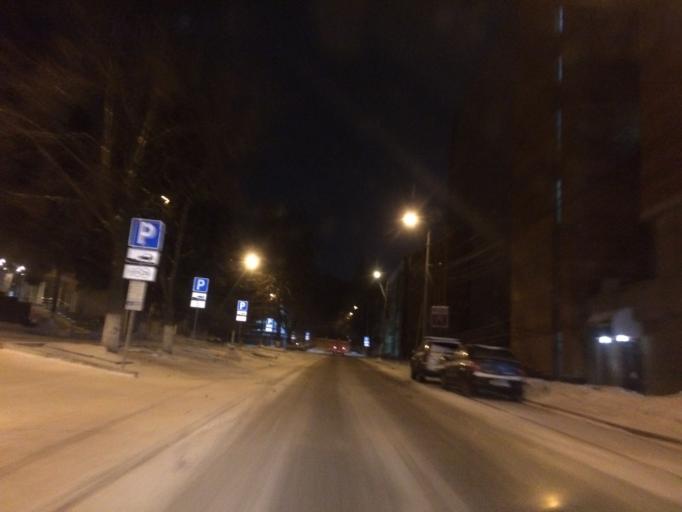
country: RU
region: Tula
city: Tula
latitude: 54.1841
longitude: 37.6113
